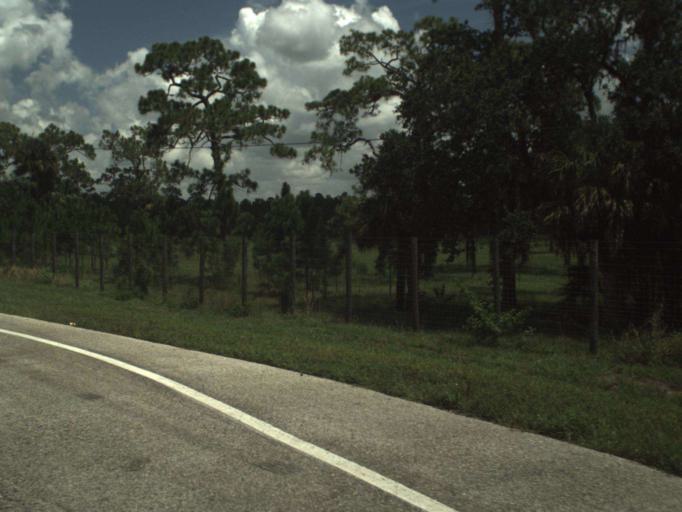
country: US
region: Florida
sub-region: Indian River County
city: Fellsmere
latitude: 27.6689
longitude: -80.8021
